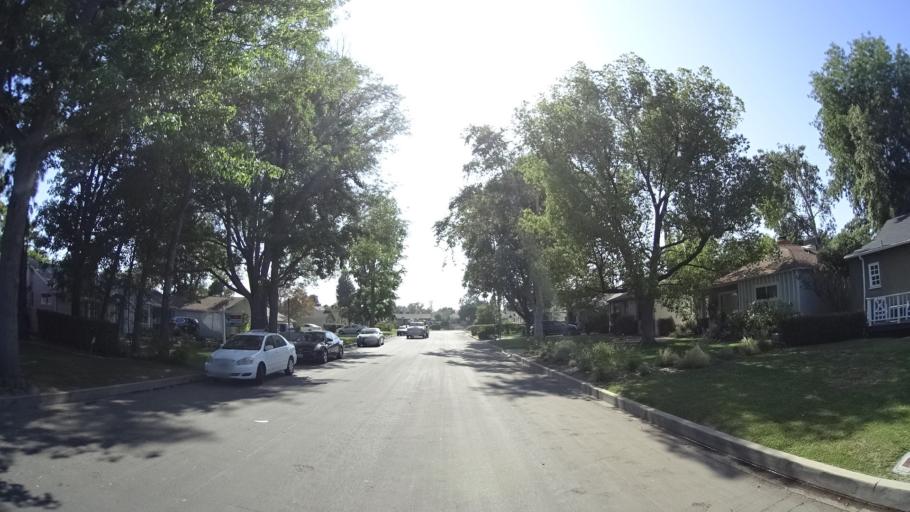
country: US
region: California
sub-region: Los Angeles County
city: Van Nuys
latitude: 34.1694
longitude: -118.4542
